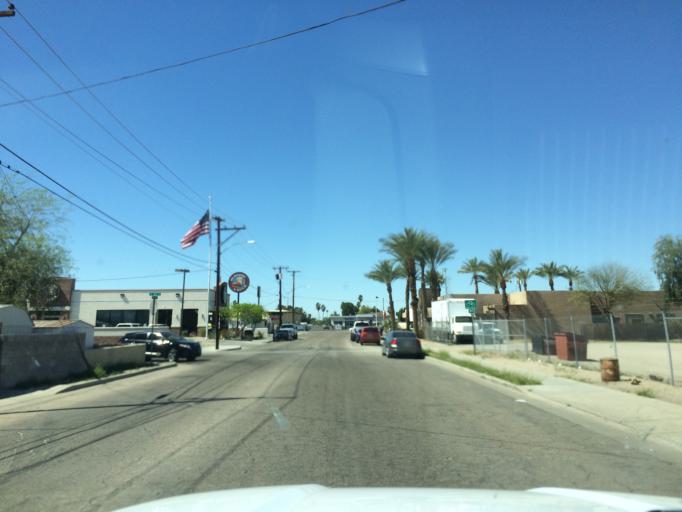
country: US
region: Arizona
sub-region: Yuma County
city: Yuma
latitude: 32.6913
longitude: -114.6228
